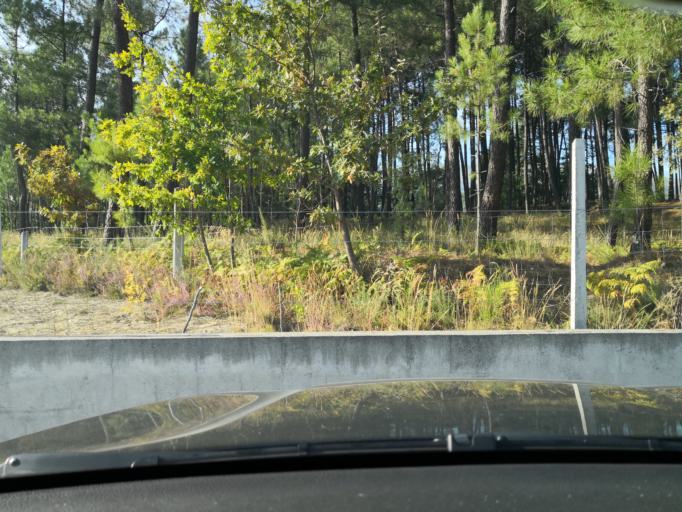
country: PT
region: Vila Real
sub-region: Vila Real
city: Vila Real
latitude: 41.3306
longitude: -7.7392
